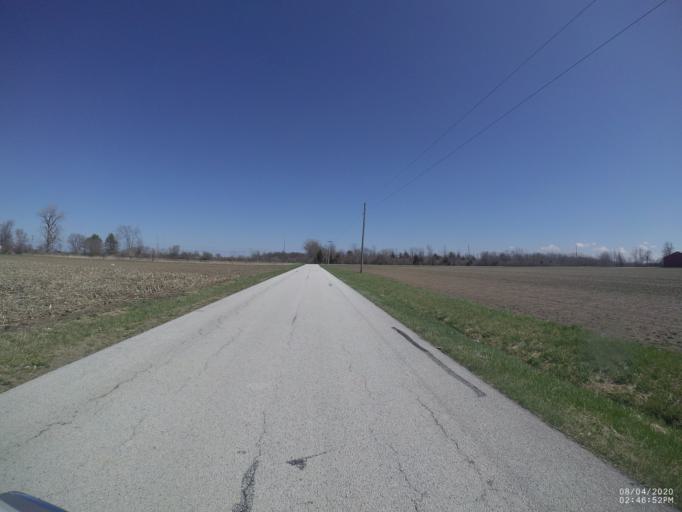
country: US
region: Ohio
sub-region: Sandusky County
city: Gibsonburg
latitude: 41.2974
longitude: -83.2754
